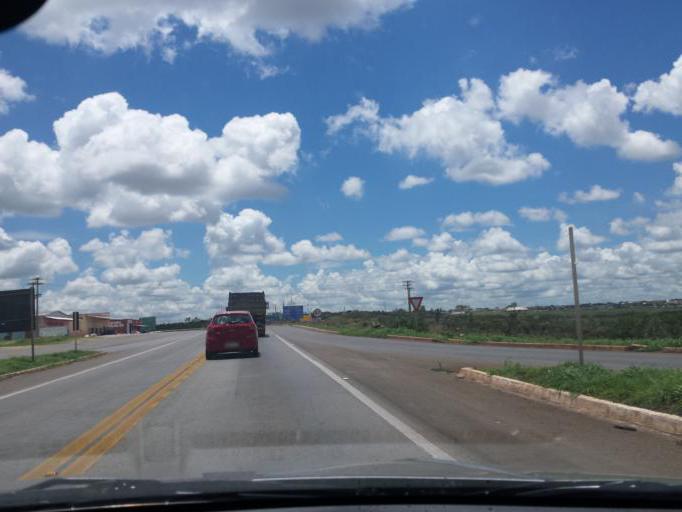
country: BR
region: Goias
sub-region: Cristalina
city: Cristalina
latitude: -16.7343
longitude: -47.6213
